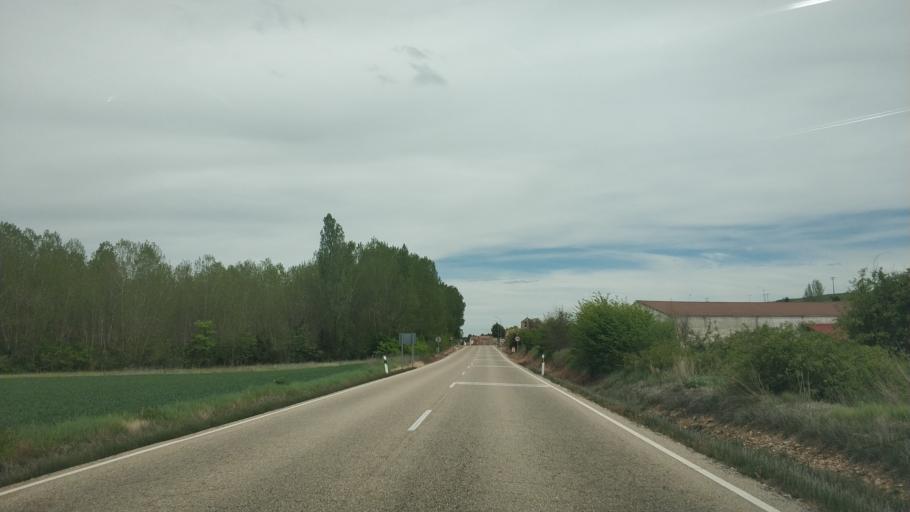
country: ES
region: Castille and Leon
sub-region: Provincia de Soria
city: Valdenebro
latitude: 41.5721
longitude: -3.0147
